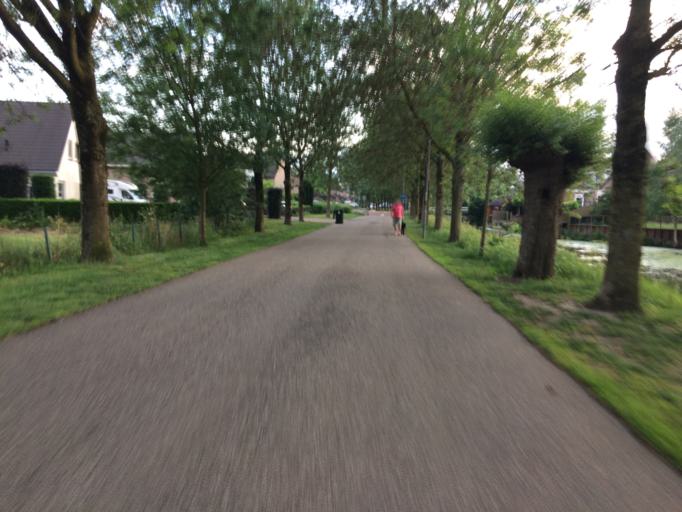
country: NL
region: North Brabant
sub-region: Gemeente 's-Hertogenbosch
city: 's-Hertogenbosch
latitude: 51.7318
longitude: 5.3094
